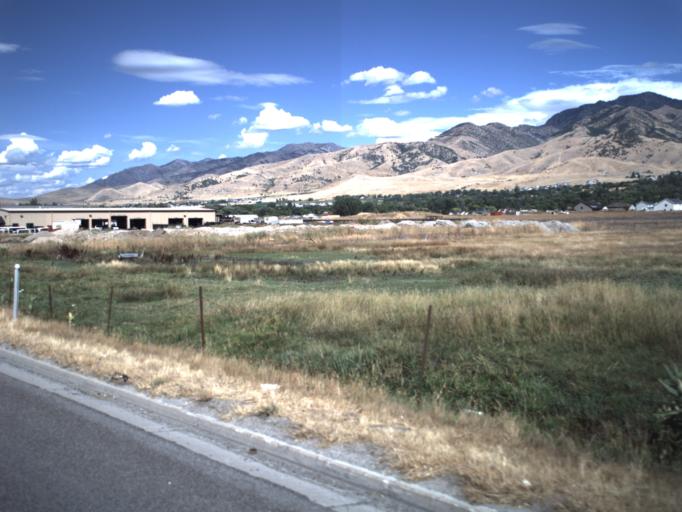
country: US
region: Utah
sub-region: Cache County
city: Hyde Park
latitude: 41.7896
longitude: -111.8336
